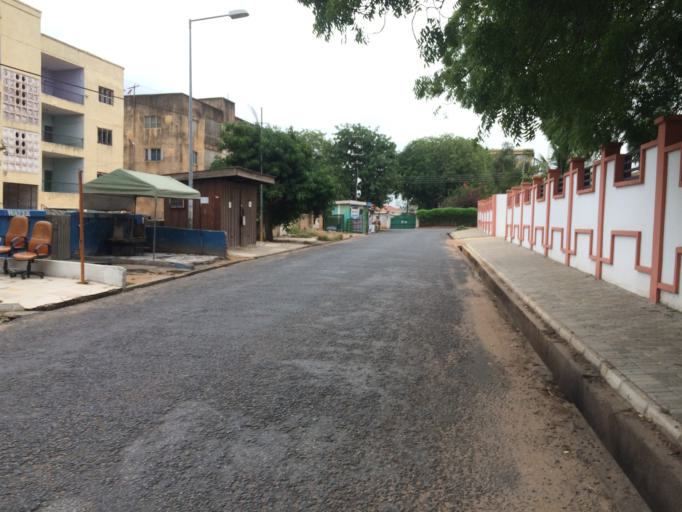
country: GH
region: Greater Accra
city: Accra
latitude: 5.5590
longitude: -0.1851
